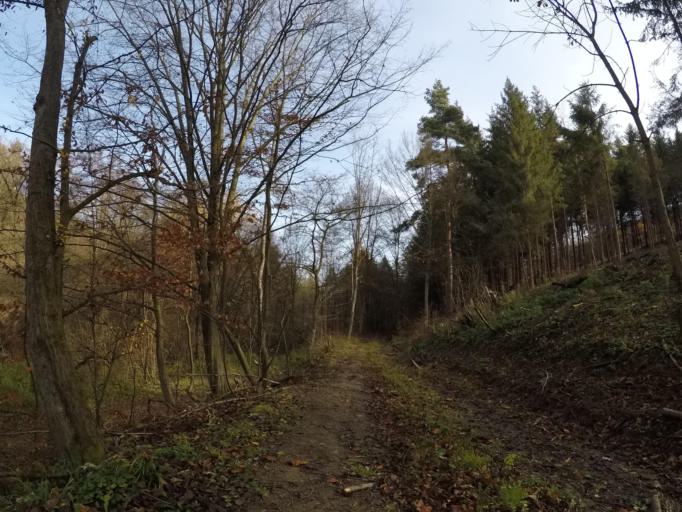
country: SK
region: Presovsky
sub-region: Okres Presov
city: Presov
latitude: 48.9166
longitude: 21.2059
